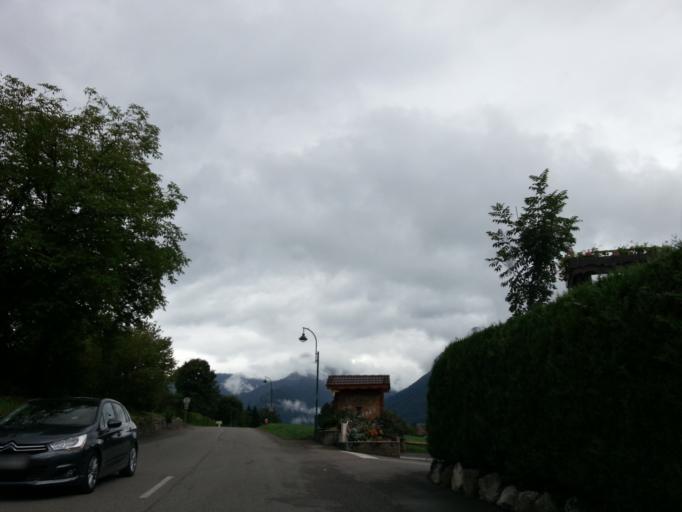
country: FR
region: Rhone-Alpes
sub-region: Departement de la Haute-Savoie
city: Doussard
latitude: 45.8007
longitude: 6.2047
